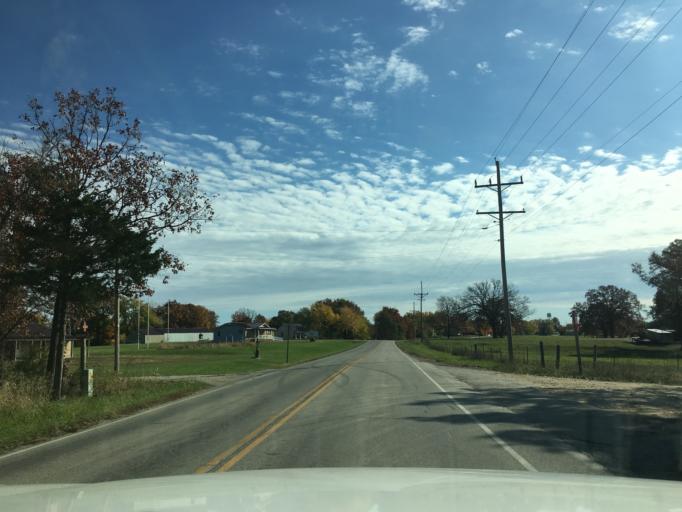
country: US
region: Missouri
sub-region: Maries County
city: Belle
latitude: 38.2969
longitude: -91.7227
